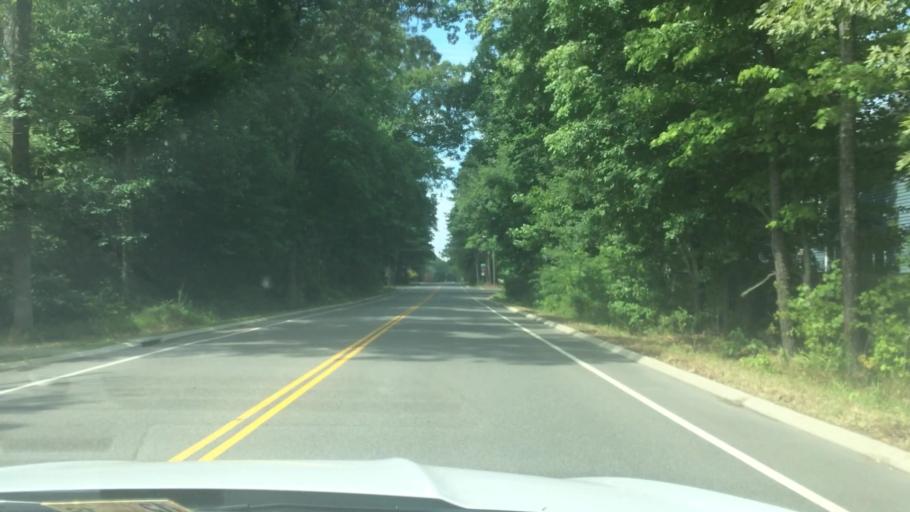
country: US
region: Virginia
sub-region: City of Poquoson
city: Poquoson
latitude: 37.1574
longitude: -76.4441
